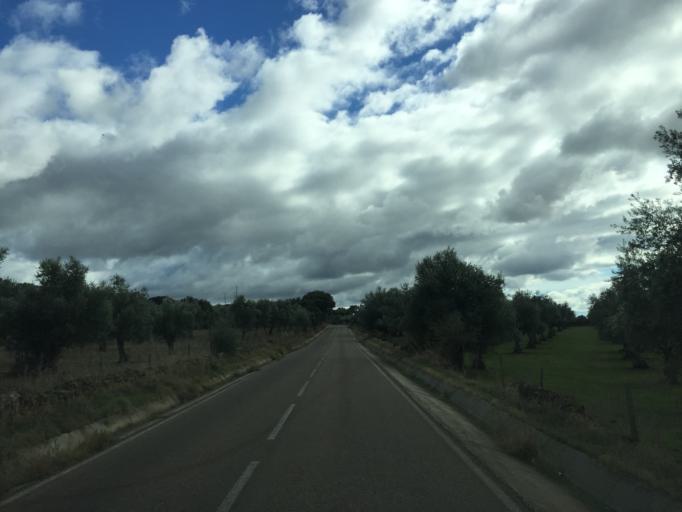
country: PT
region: Portalegre
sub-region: Alter do Chao
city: Alter do Chao
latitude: 39.2191
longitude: -7.6710
